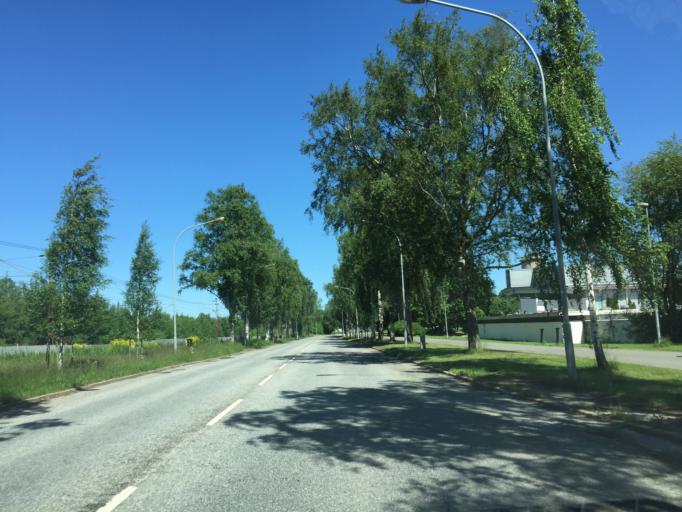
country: SE
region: OErebro
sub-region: Orebro Kommun
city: Orebro
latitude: 59.2598
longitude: 15.1906
